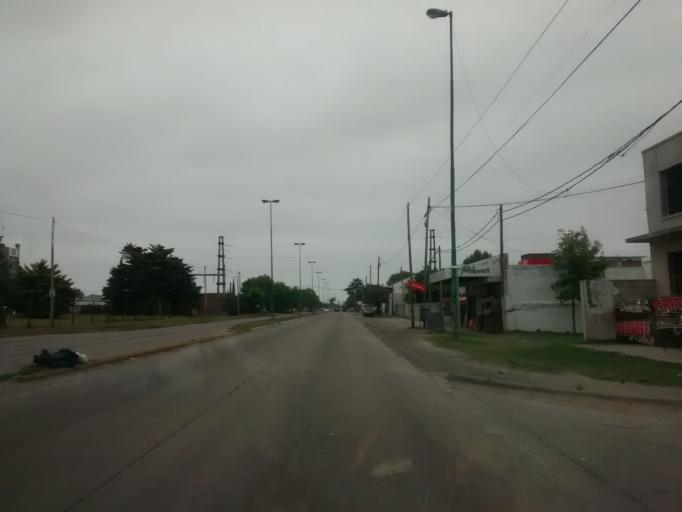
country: AR
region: Buenos Aires
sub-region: Partido de La Plata
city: La Plata
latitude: -34.9811
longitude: -58.0327
